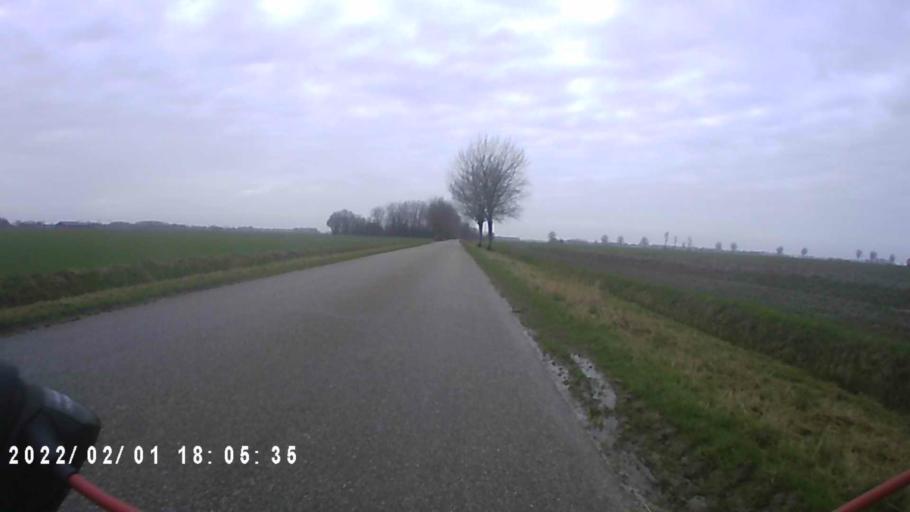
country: NL
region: Groningen
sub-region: Gemeente De Marne
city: Ulrum
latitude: 53.3401
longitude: 6.3687
